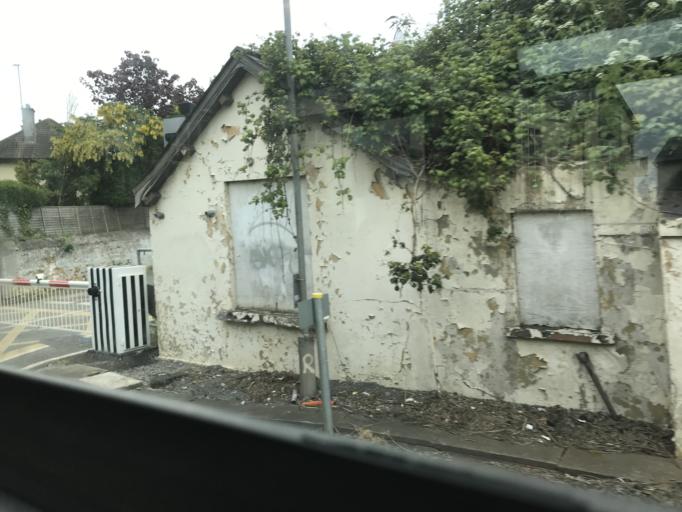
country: IE
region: Leinster
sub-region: Fingal County
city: Howth
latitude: 53.3909
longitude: -6.0846
